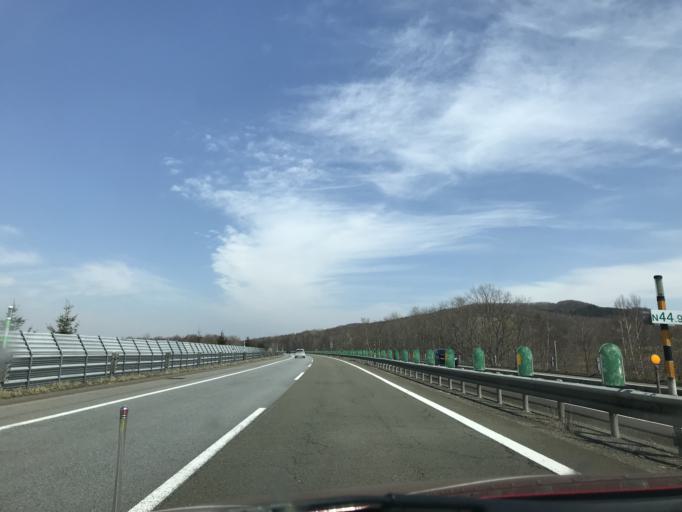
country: JP
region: Hokkaido
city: Bibai
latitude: 43.2687
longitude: 141.8449
